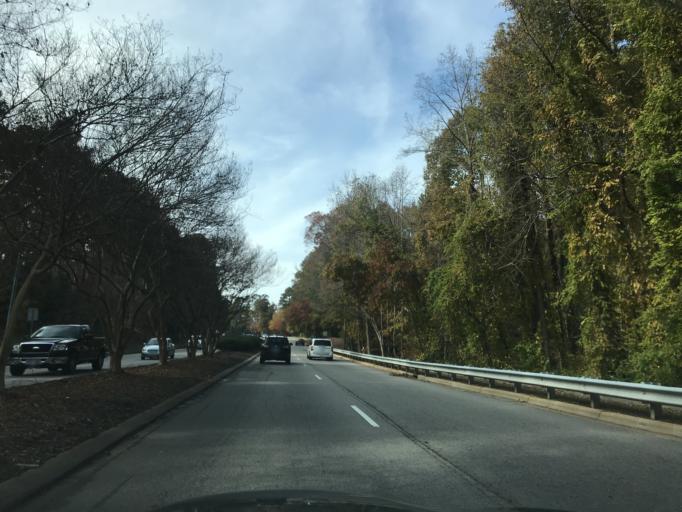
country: US
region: North Carolina
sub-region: Wake County
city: West Raleigh
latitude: 35.8570
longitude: -78.6639
